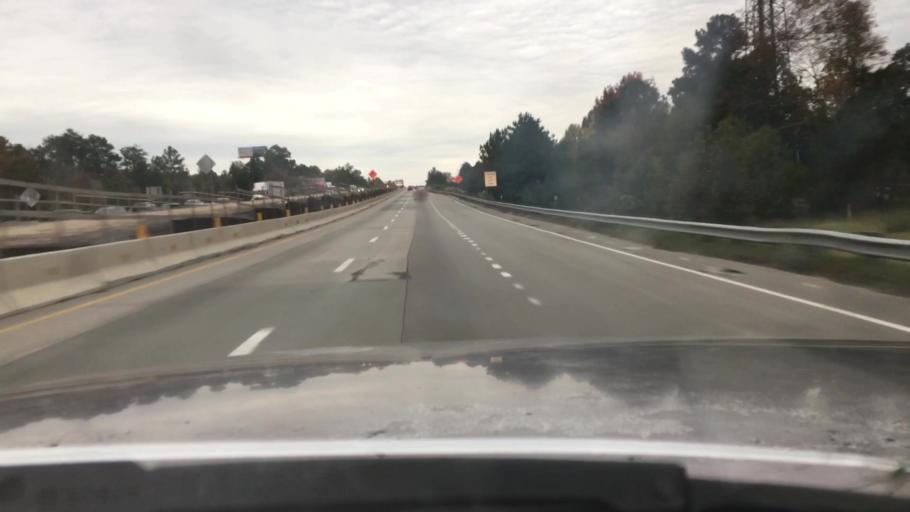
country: US
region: South Carolina
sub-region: Lexington County
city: Lexington
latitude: 33.9764
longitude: -81.1960
